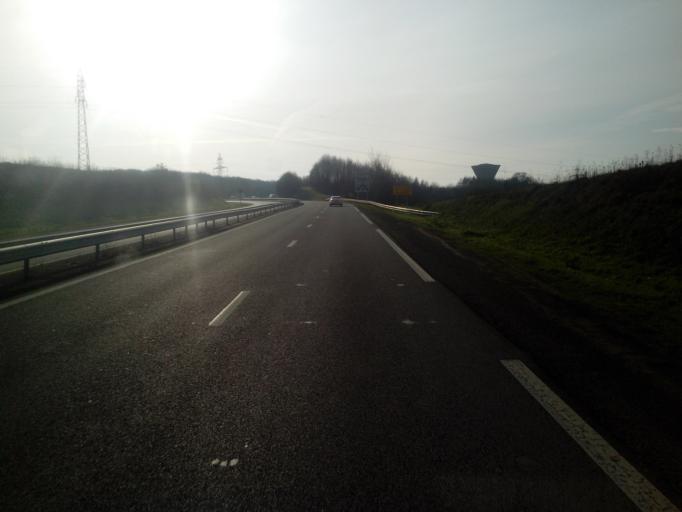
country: FR
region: Brittany
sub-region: Departement d'Ille-et-Vilaine
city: Cesson-Sevigne
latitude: 48.1436
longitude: -1.6265
